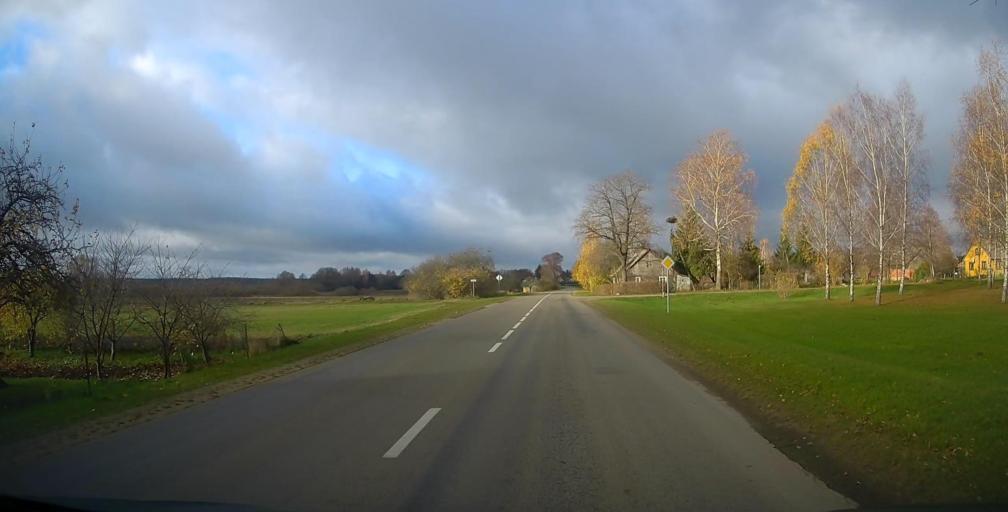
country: LT
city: Kybartai
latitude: 54.4545
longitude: 22.7299
